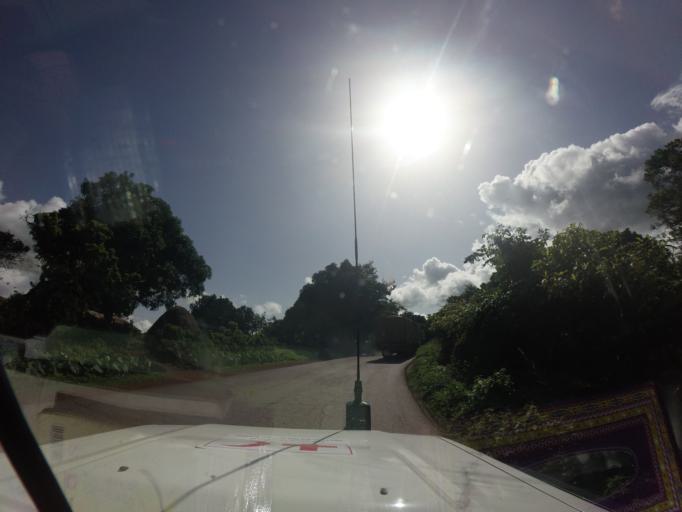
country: GN
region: Mamou
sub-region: Mamou Prefecture
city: Mamou
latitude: 10.3160
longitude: -12.2554
